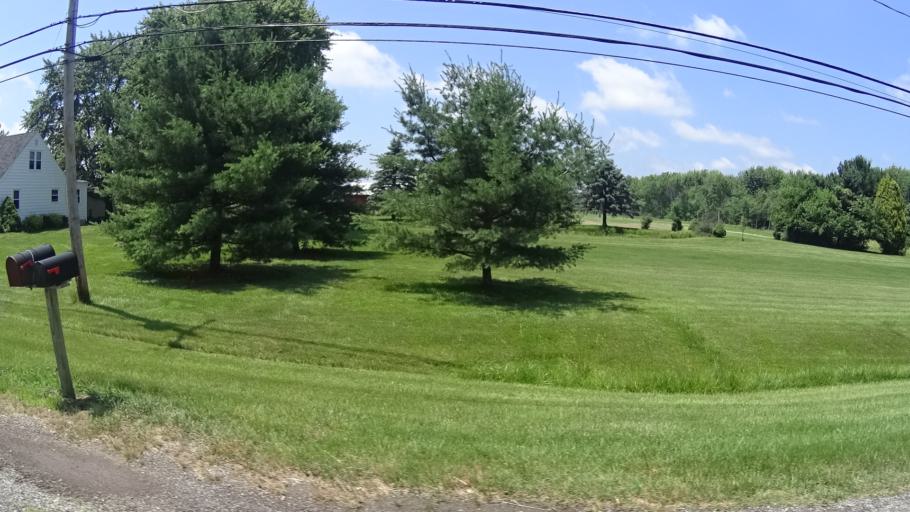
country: US
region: Ohio
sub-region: Lorain County
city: Vermilion
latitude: 41.3479
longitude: -82.3597
